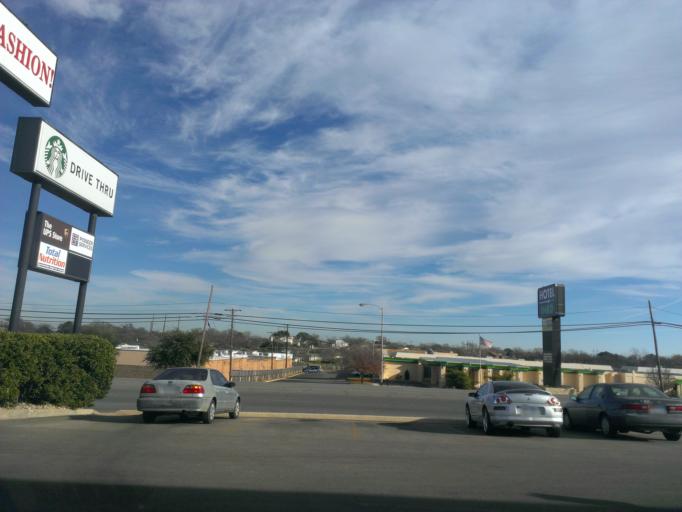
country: US
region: Texas
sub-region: Bell County
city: Killeen
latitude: 31.1114
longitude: -97.7472
